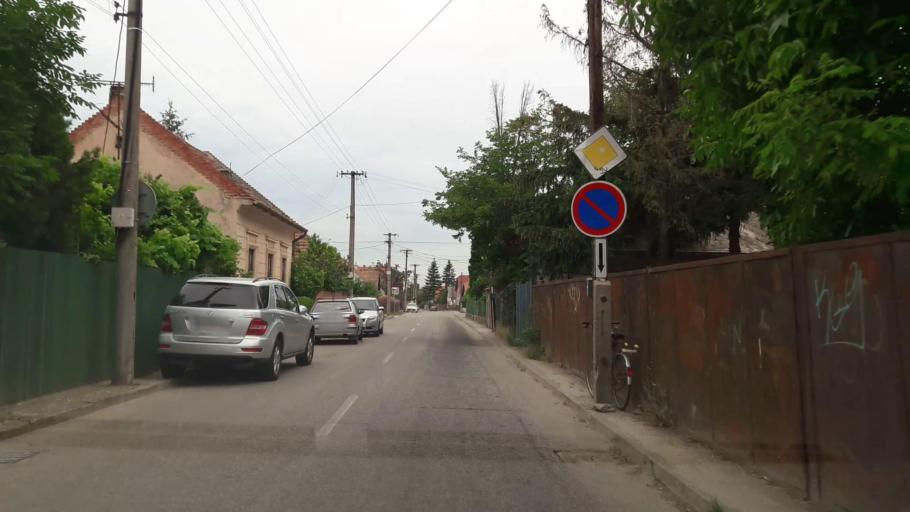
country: SK
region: Bratislavsky
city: Senec
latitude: 48.2085
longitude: 17.3613
